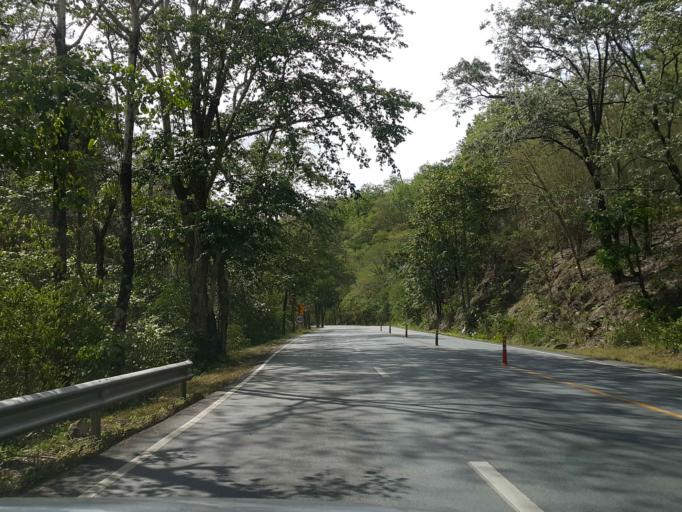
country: TH
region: Tak
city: Tak
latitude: 16.8094
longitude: 98.9835
